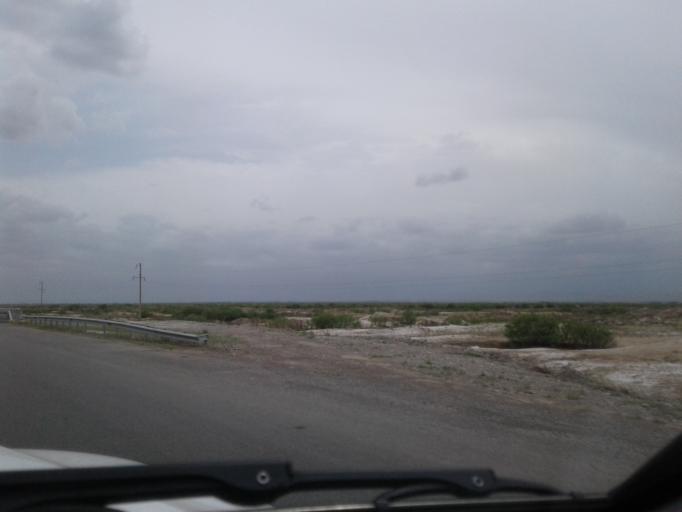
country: TM
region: Ahal
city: Kaka
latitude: 37.5217
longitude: 59.4275
